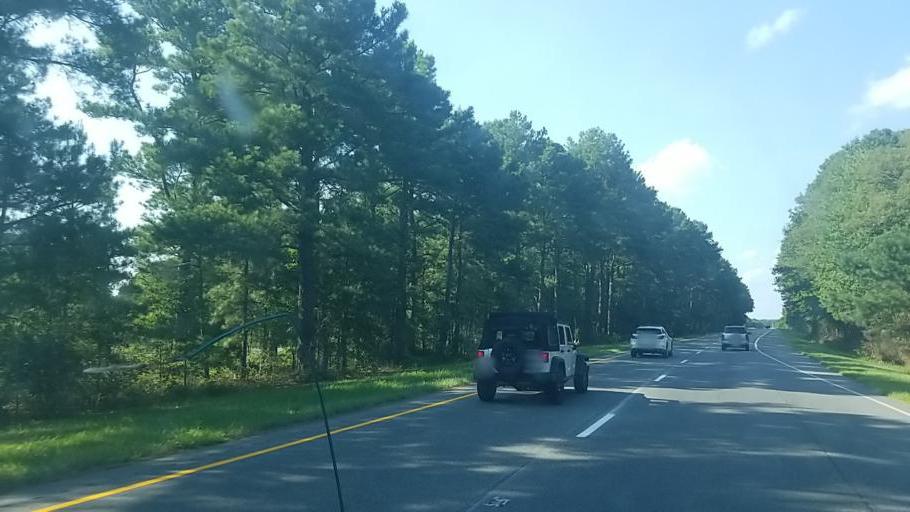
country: US
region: Maryland
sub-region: Worcester County
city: Berlin
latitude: 38.3496
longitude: -75.2146
